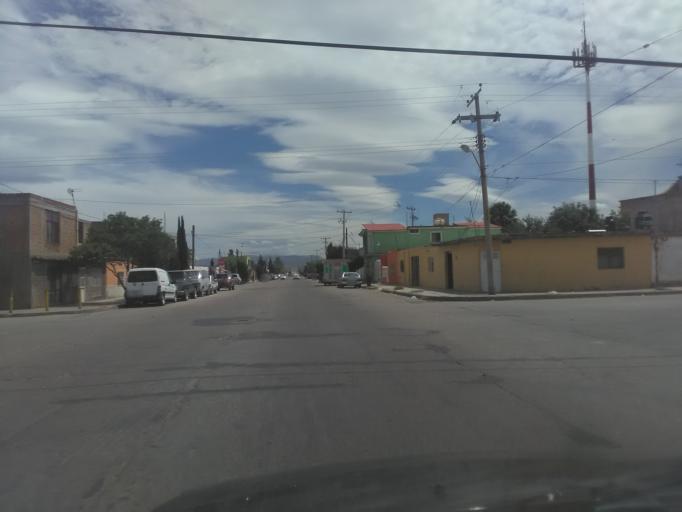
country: MX
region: Durango
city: Victoria de Durango
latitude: 24.0232
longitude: -104.6312
